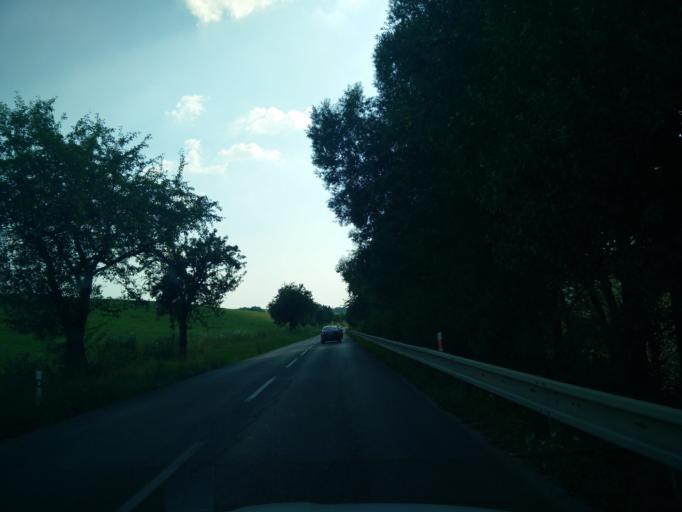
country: SK
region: Zilinsky
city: Rajec
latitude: 49.1196
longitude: 18.6599
